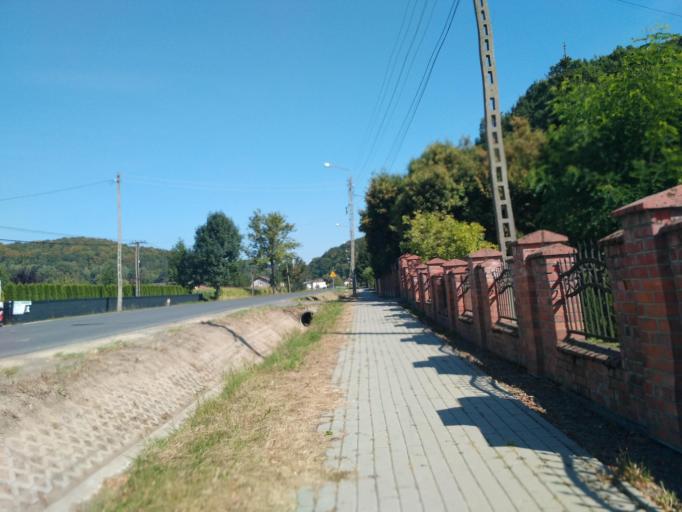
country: PL
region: Subcarpathian Voivodeship
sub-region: Powiat brzozowski
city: Grabownica Starzenska
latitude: 49.6628
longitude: 22.0809
